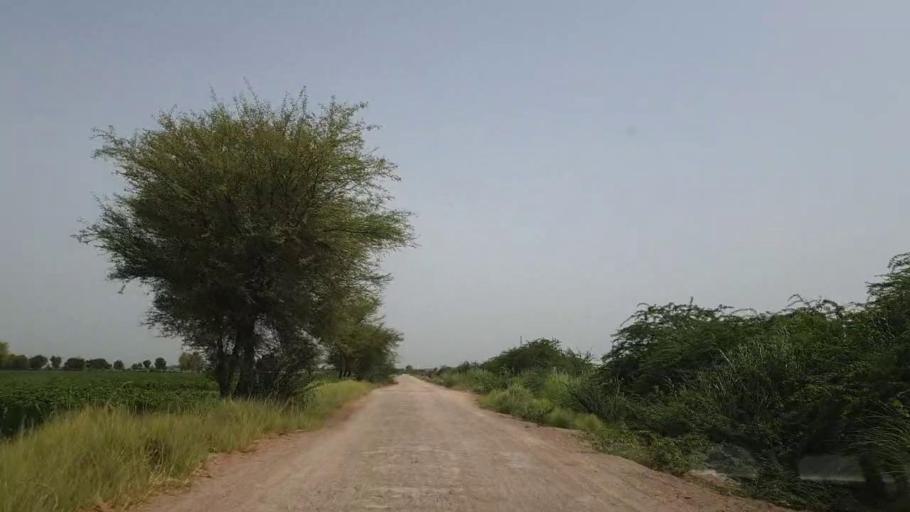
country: PK
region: Sindh
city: Sakrand
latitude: 26.1364
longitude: 68.3642
